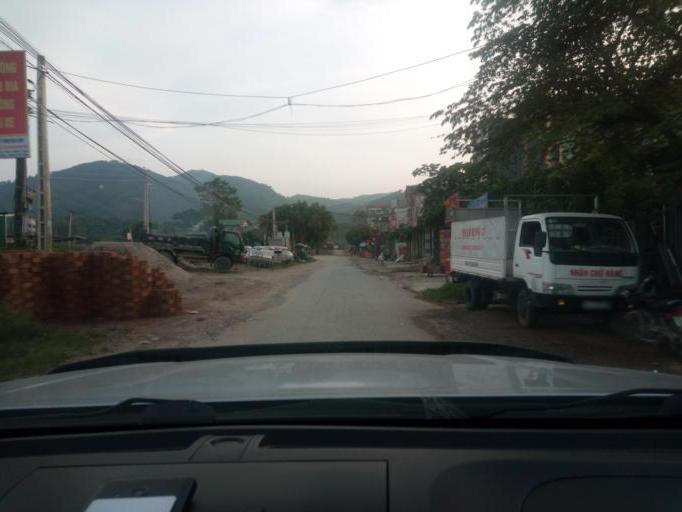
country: VN
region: Yen Bai
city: Co Phuc
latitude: 21.8631
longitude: 104.6404
